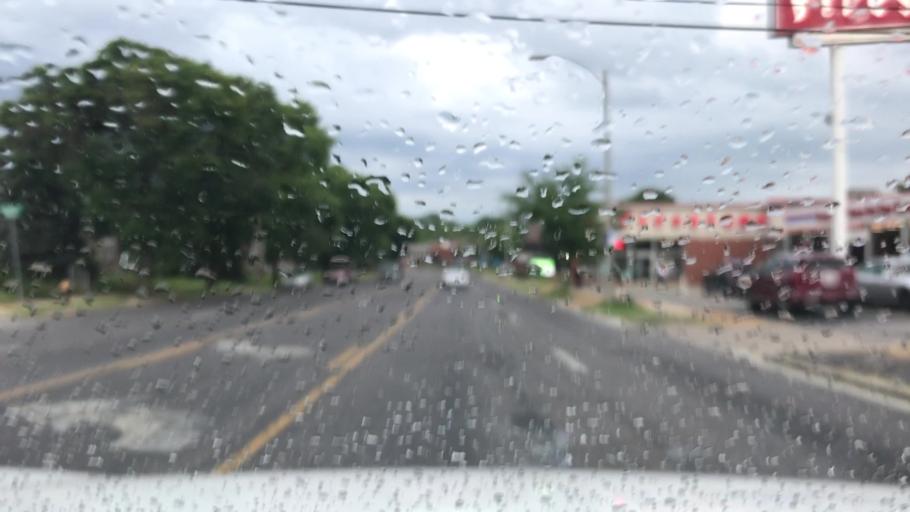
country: US
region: Missouri
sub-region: Saint Louis County
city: Maplewood
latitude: 38.5936
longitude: -90.2960
